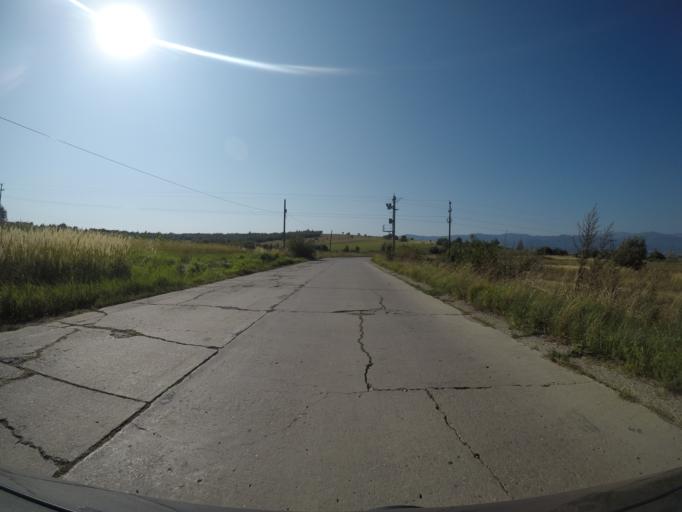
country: RO
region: Brasov
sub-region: Comuna Sinca Veche
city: Persani
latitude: 45.7791
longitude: 25.1919
